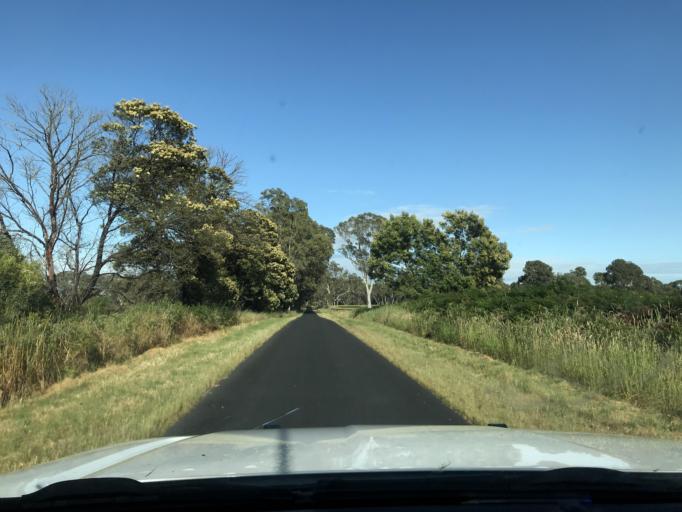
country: AU
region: South Australia
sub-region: Wattle Range
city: Penola
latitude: -37.2003
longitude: 140.9775
